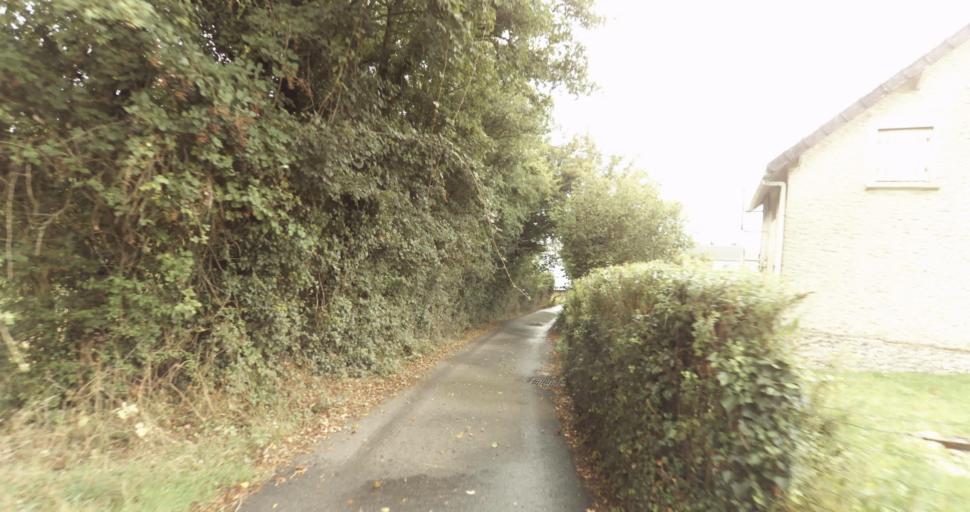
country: FR
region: Lower Normandy
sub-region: Departement de l'Orne
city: Sainte-Gauburge-Sainte-Colombe
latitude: 48.7129
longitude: 0.4332
